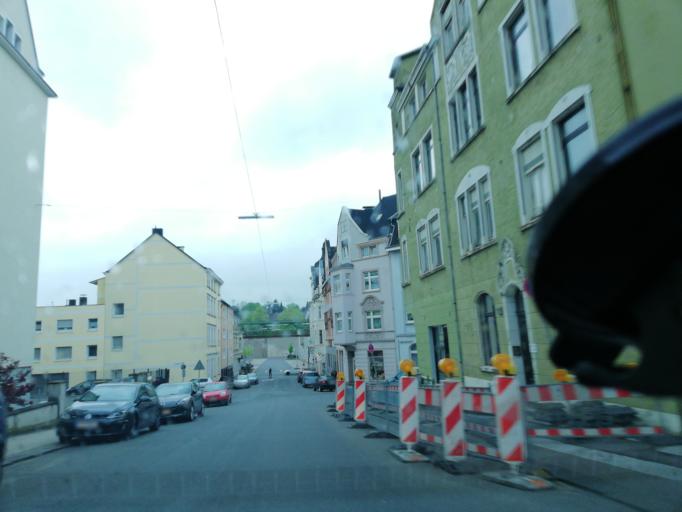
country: DE
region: North Rhine-Westphalia
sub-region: Regierungsbezirk Dusseldorf
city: Solingen
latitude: 51.2318
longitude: 7.0744
